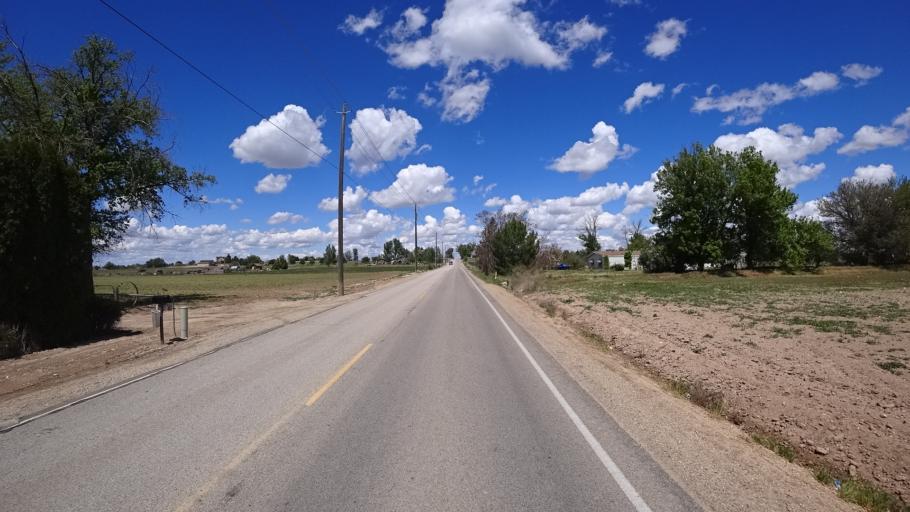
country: US
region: Idaho
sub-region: Ada County
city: Kuna
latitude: 43.5527
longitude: -116.4338
